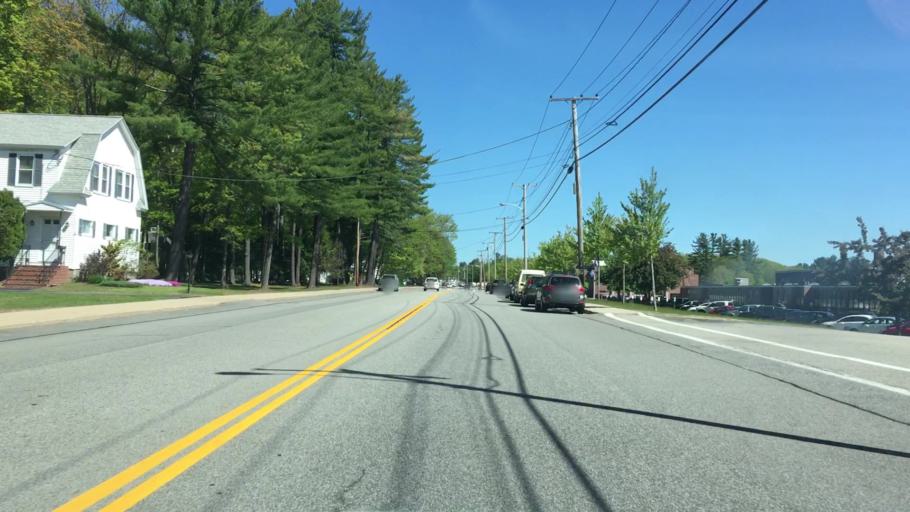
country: US
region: Maine
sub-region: York County
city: Sanford (historical)
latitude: 43.4488
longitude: -70.7871
